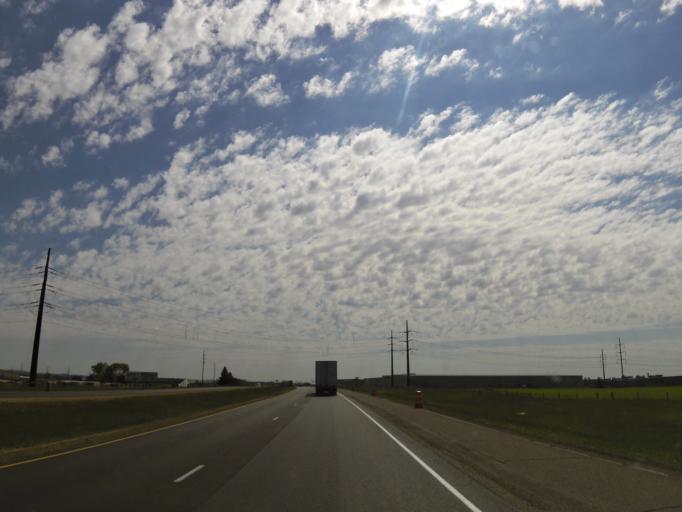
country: US
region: Wisconsin
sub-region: Dunn County
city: Menomonie
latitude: 44.9050
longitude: -91.8766
